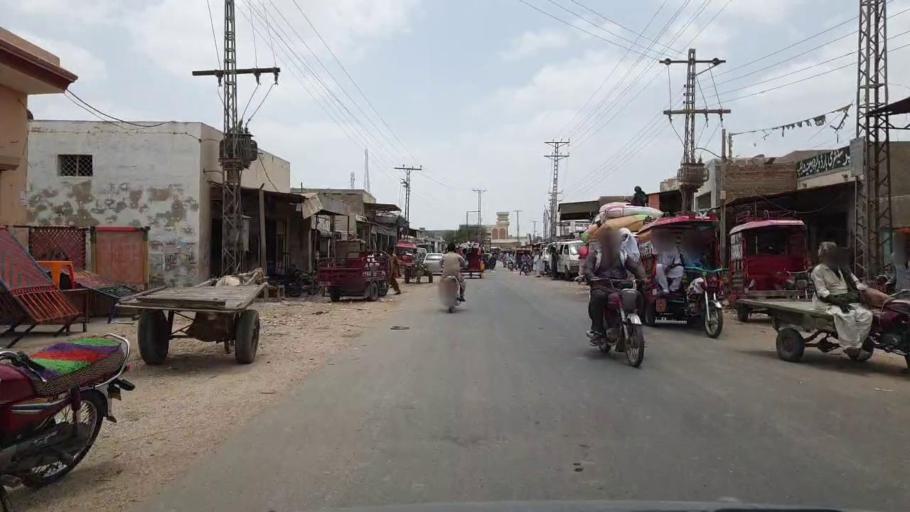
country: PK
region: Sindh
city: Naukot
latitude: 24.8538
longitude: 69.4048
